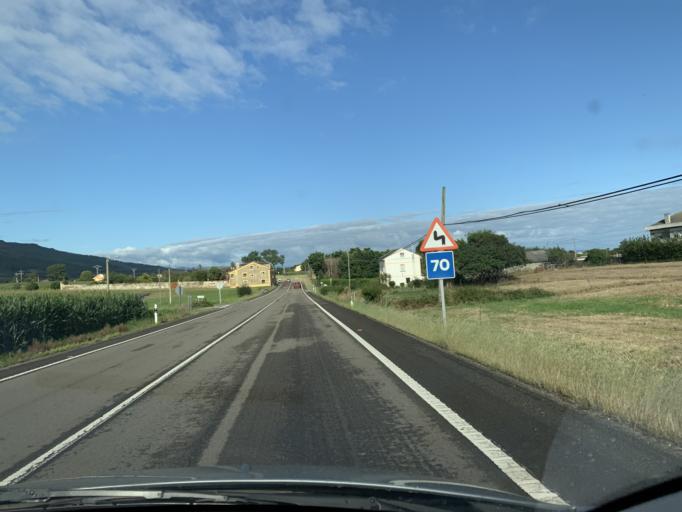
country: ES
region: Galicia
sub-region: Provincia de Lugo
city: Ribadeo
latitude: 43.5470
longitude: -7.1149
